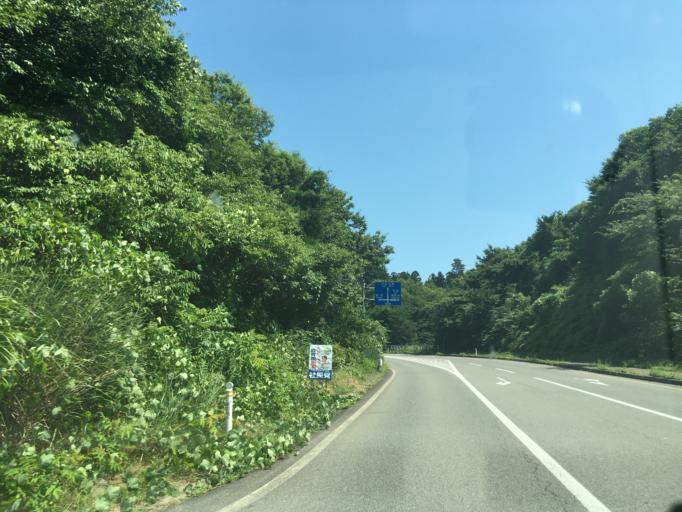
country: JP
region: Akita
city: Tenno
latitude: 39.9680
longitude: 139.7509
